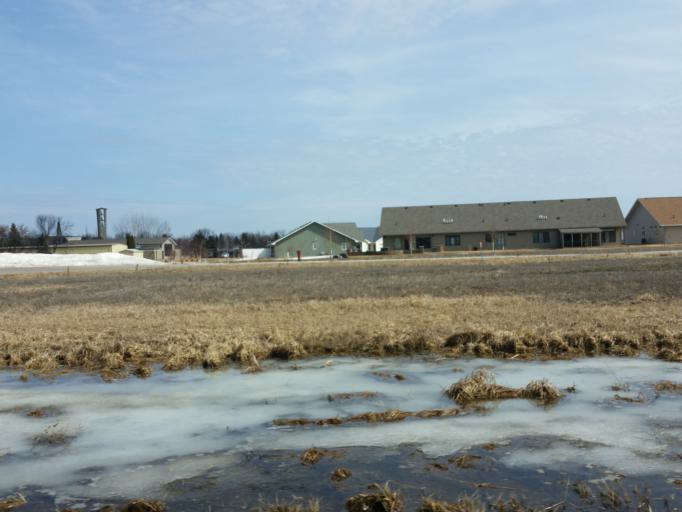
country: US
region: North Dakota
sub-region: Walsh County
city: Grafton
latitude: 48.4065
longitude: -97.4204
